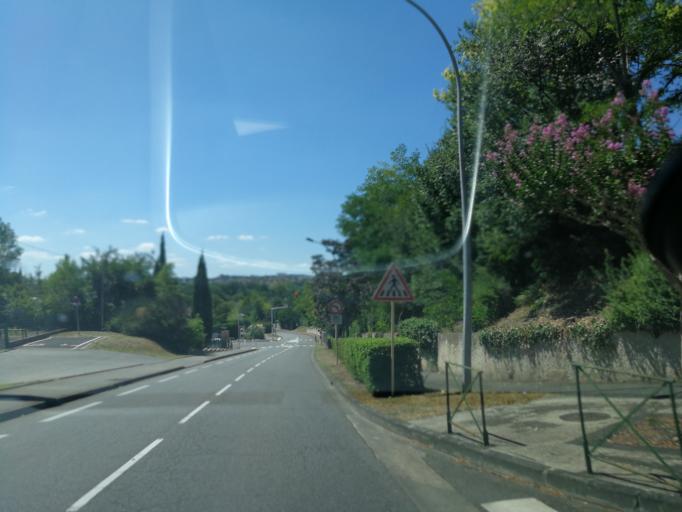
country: FR
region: Midi-Pyrenees
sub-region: Departement de la Haute-Garonne
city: Balma
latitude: 43.5988
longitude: 1.5061
